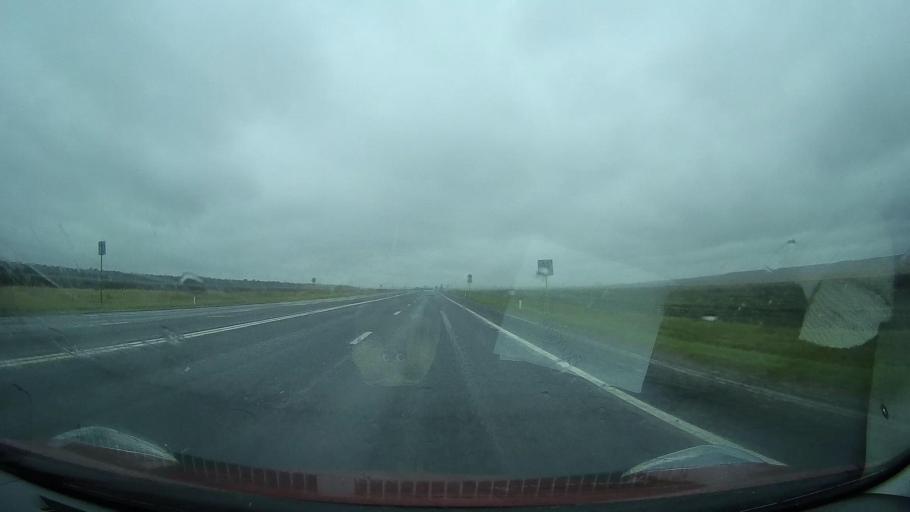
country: RU
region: Stavropol'skiy
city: Nevinnomyssk
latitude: 44.6266
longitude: 42.0525
